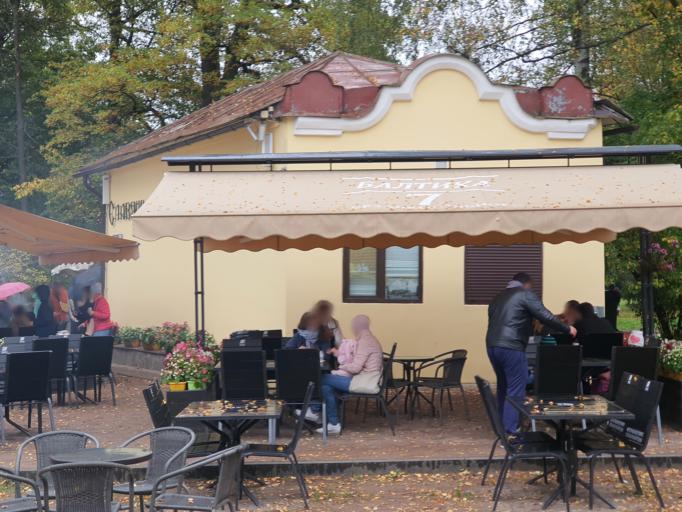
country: RU
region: St.-Petersburg
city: Pavlovsk
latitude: 59.6875
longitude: 30.4463
